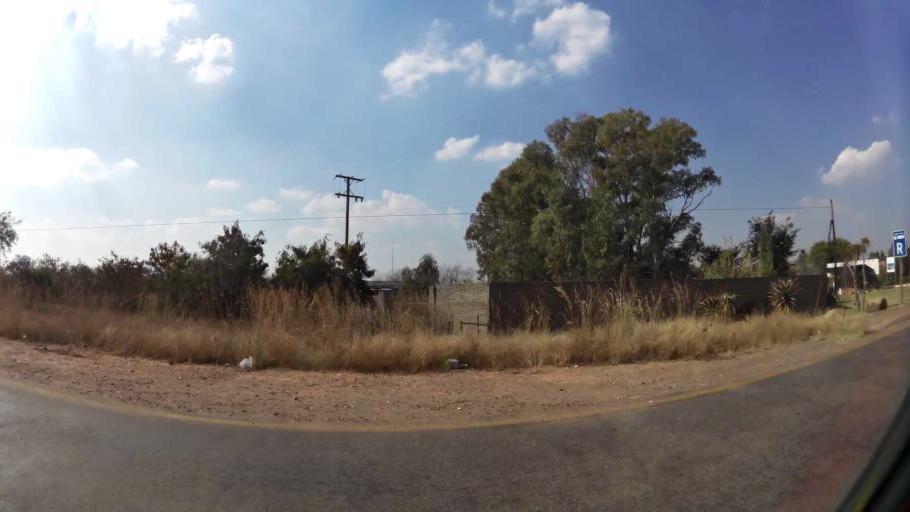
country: ZA
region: North-West
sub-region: Bojanala Platinum District Municipality
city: Rustenburg
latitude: -25.5423
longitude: 27.1244
